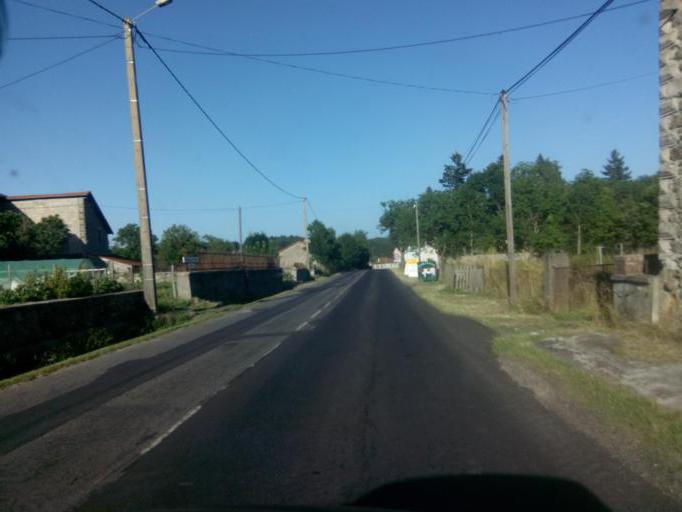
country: FR
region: Auvergne
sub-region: Departement de la Haute-Loire
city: Fontannes
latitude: 45.3050
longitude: 3.7864
